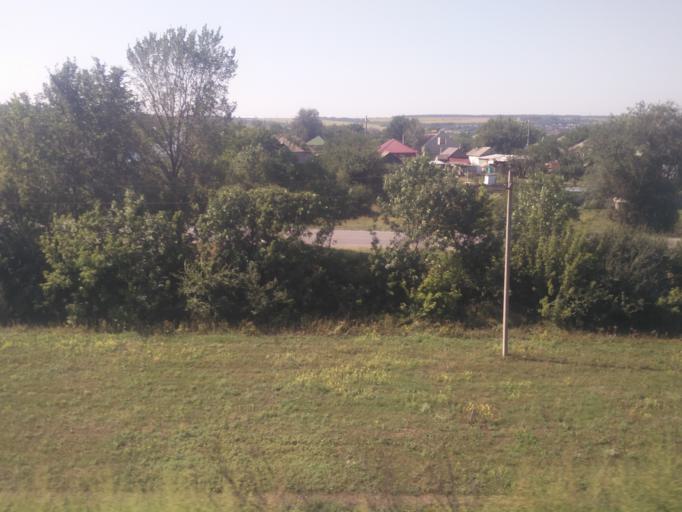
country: RU
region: Rostov
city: Krasnyy Sulin
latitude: 47.8770
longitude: 40.1115
